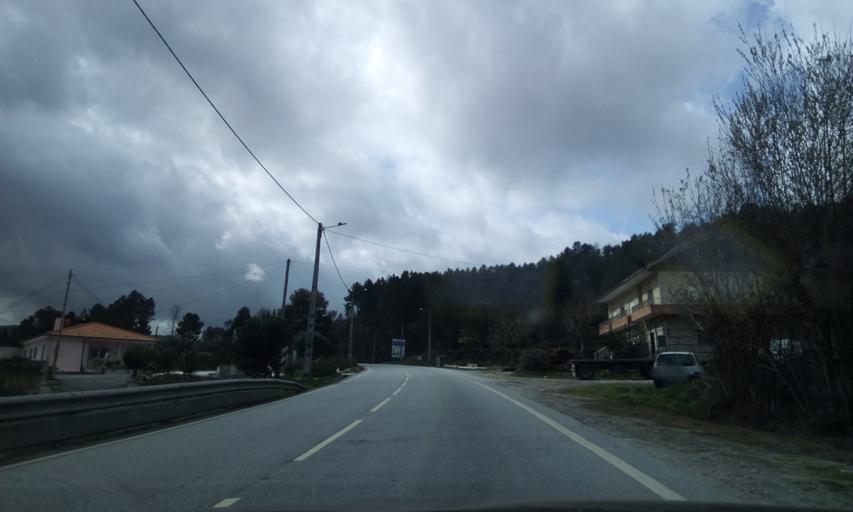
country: PT
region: Viseu
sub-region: Mangualde
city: Mangualde
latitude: 40.6418
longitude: -7.7385
